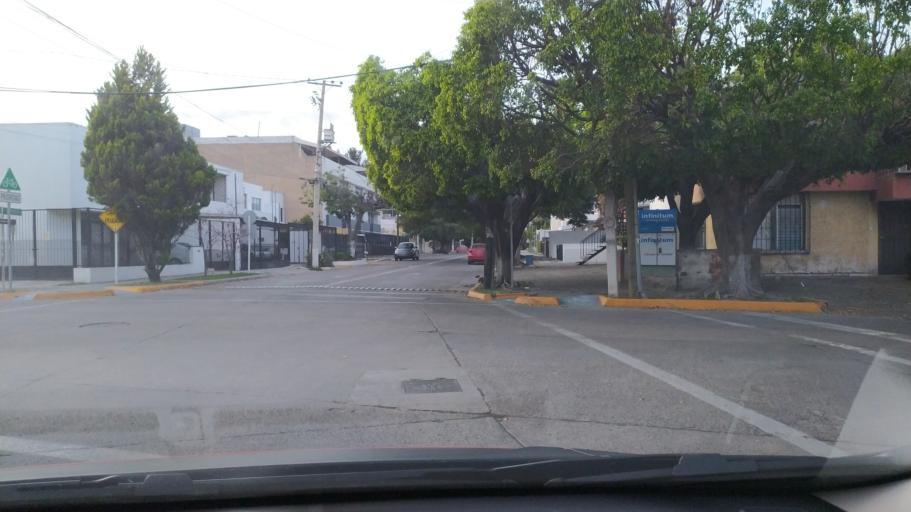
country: MX
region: Jalisco
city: Guadalajara
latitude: 20.6593
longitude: -103.4021
